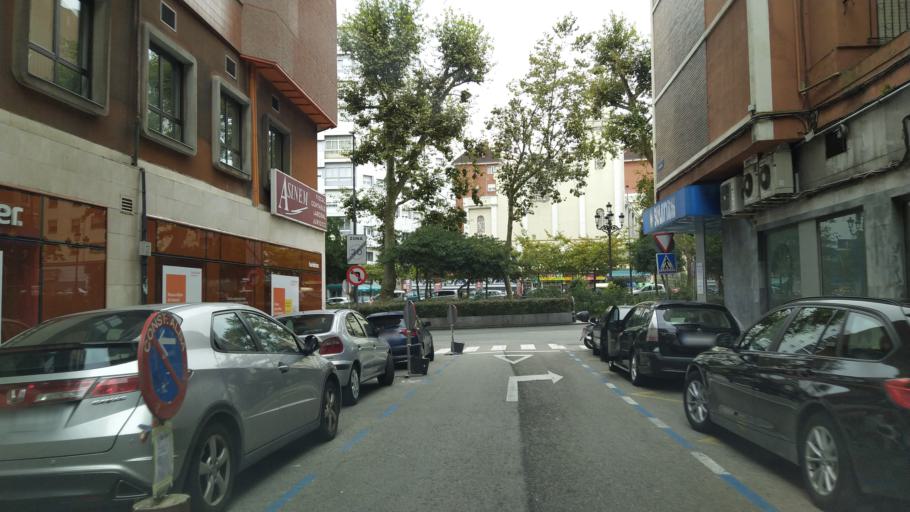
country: ES
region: Cantabria
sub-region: Provincia de Cantabria
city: Santander
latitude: 43.4593
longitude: -3.8248
